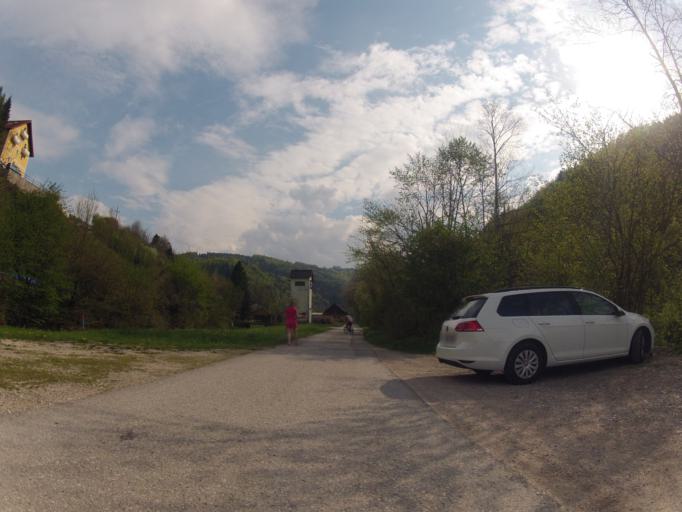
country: AT
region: Upper Austria
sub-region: Politischer Bezirk Gmunden
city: Altmunster
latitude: 47.9315
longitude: 13.7537
